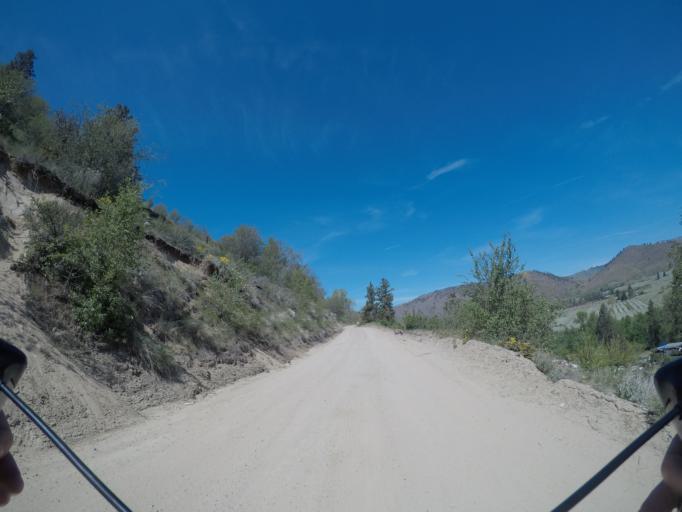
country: US
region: Washington
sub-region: Chelan County
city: Cashmere
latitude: 47.5029
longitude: -120.4430
